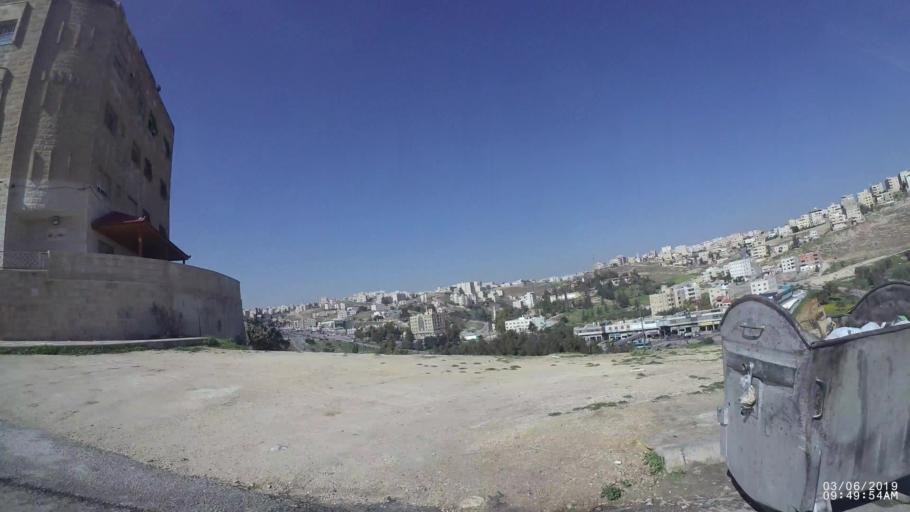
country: JO
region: Amman
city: Amman
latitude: 31.9903
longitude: 35.9816
